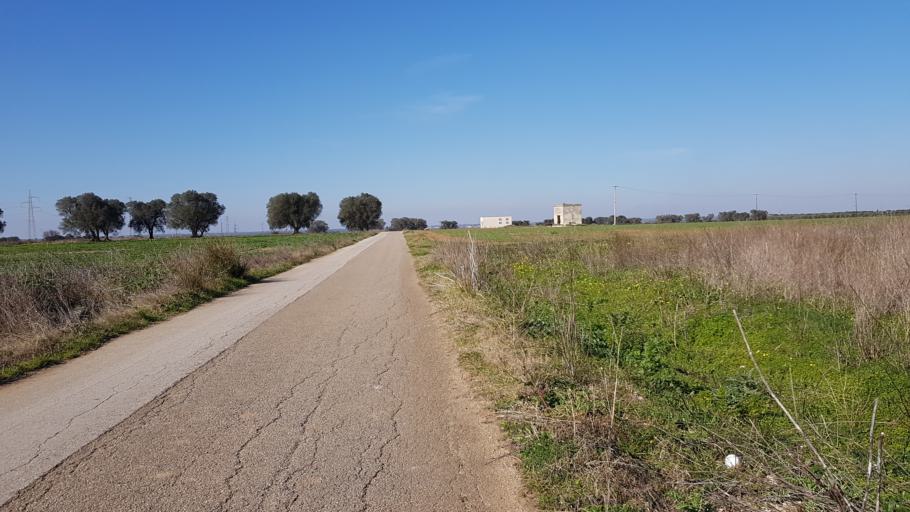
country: IT
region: Apulia
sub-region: Provincia di Brindisi
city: Mesagne
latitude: 40.6200
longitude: 17.8321
